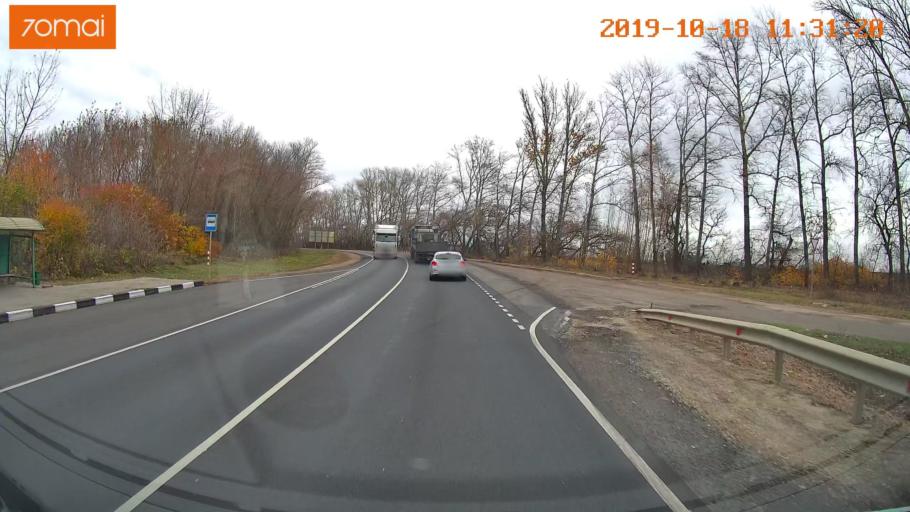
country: RU
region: Rjazan
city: Oktyabr'skiy
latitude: 54.1413
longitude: 38.6942
